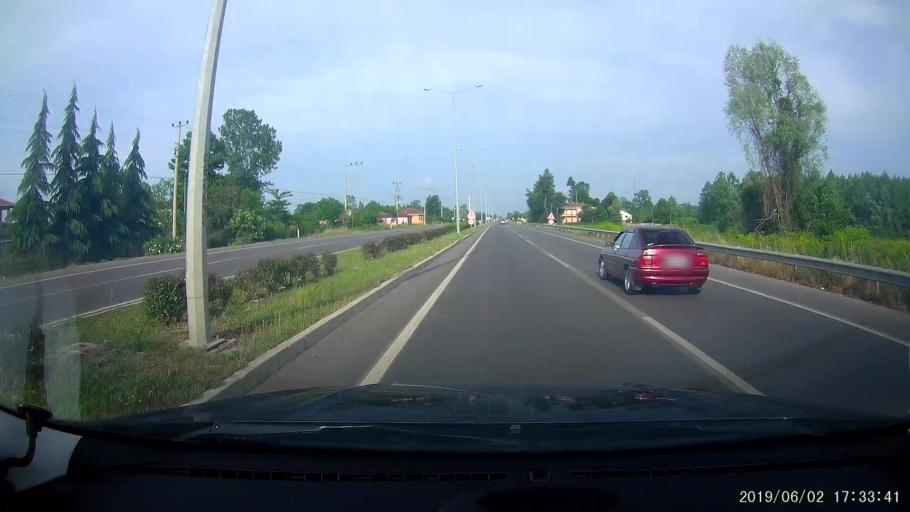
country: TR
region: Samsun
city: Terme
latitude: 41.2208
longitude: 36.8539
